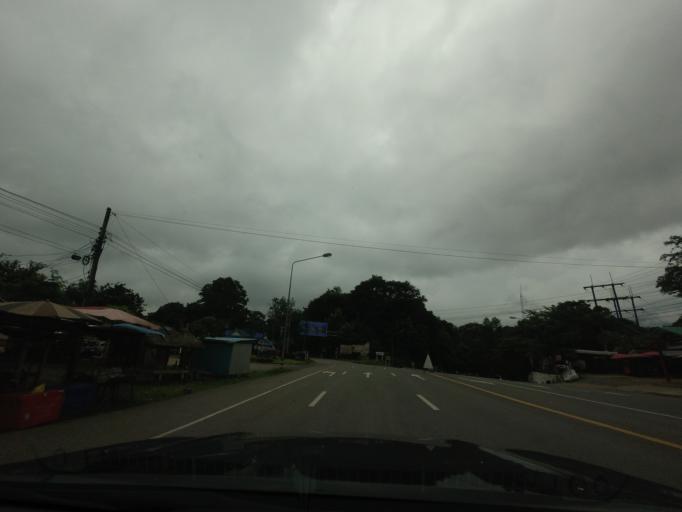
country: TH
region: Nong Khai
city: Sangkhom
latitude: 18.0270
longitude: 102.3656
